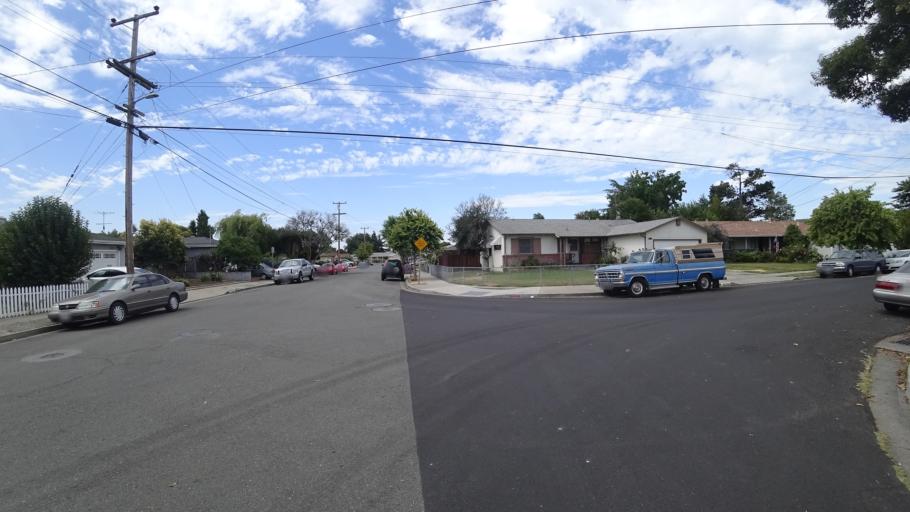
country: US
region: California
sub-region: Alameda County
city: Hayward
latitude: 37.6441
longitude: -122.0785
